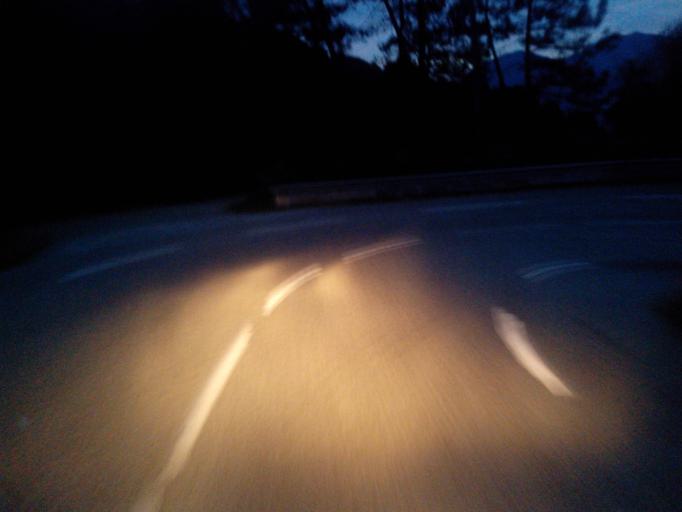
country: FR
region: Languedoc-Roussillon
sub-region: Departement du Gard
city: Saint-Jean-du-Gard
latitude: 44.1252
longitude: 3.8670
